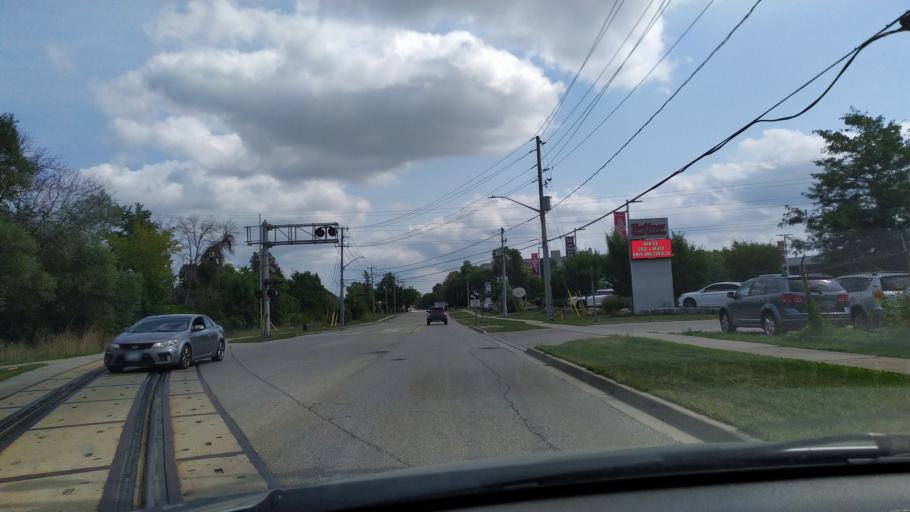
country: CA
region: Ontario
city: Kitchener
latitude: 43.4278
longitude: -80.4302
